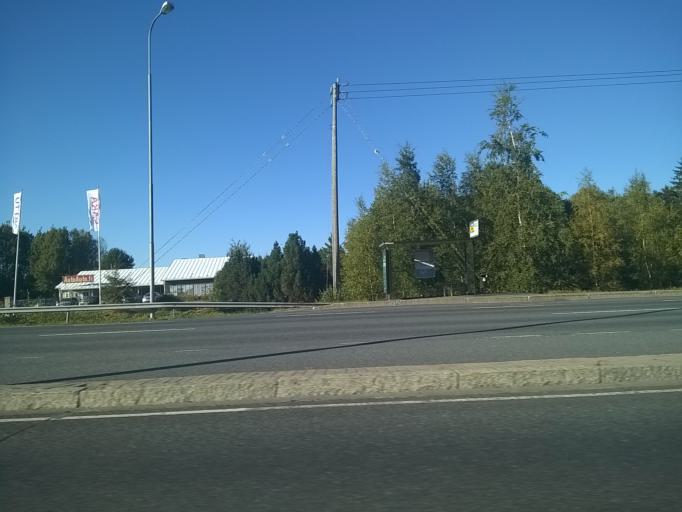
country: FI
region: Pirkanmaa
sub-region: Tampere
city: Tampere
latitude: 61.5032
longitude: 23.8628
